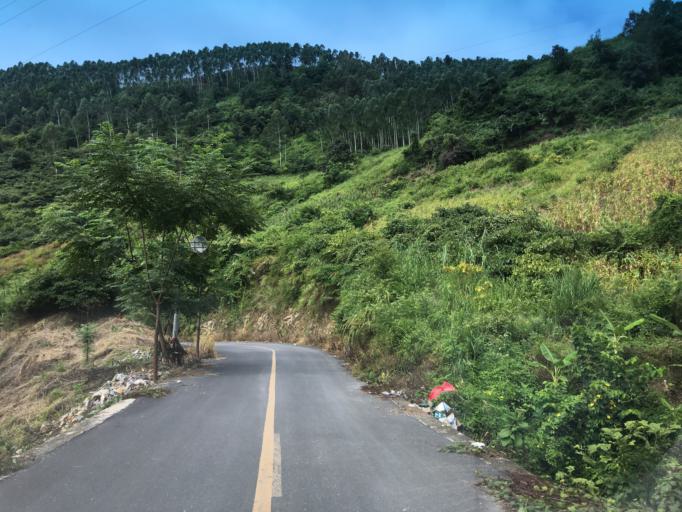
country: CN
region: Guangxi Zhuangzu Zizhiqu
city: Xinzhou
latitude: 24.8185
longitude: 105.6414
